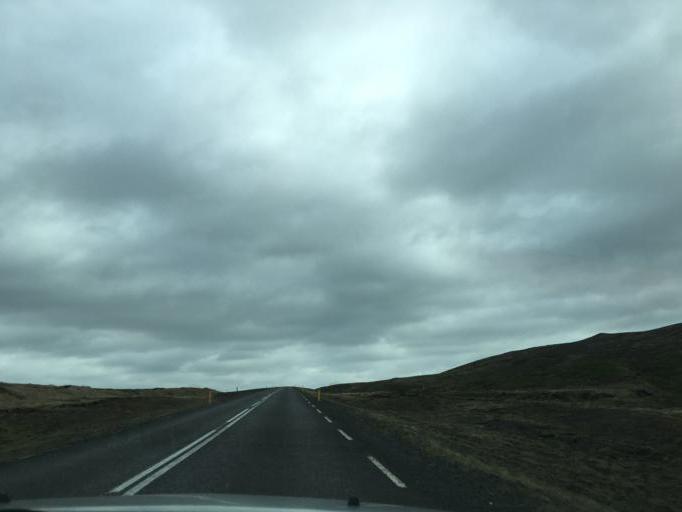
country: IS
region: South
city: Vestmannaeyjar
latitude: 64.2523
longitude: -20.2027
